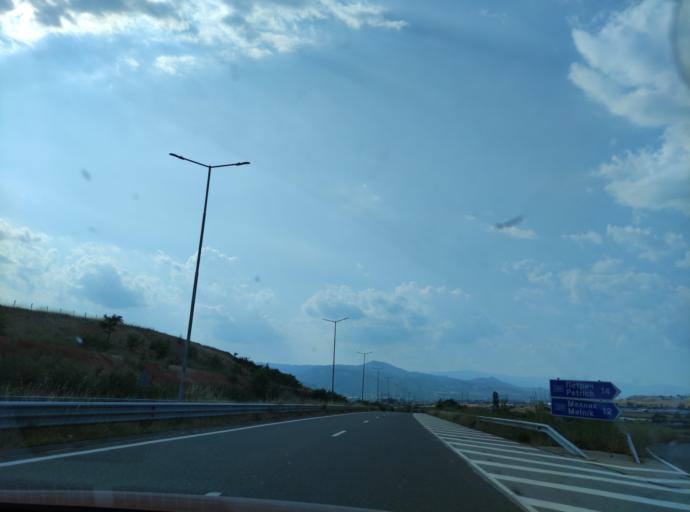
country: BG
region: Blagoevgrad
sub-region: Obshtina Sandanski
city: Sandanski
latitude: 41.4959
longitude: 23.2850
